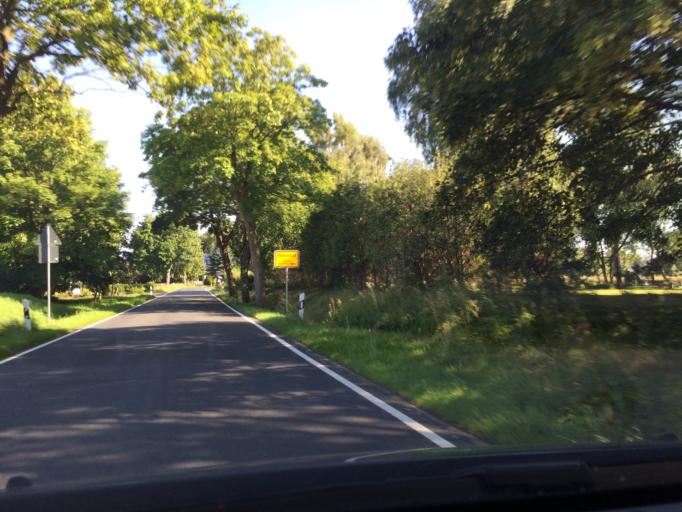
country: DE
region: Mecklenburg-Vorpommern
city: Velgast
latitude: 54.3356
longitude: 12.7961
